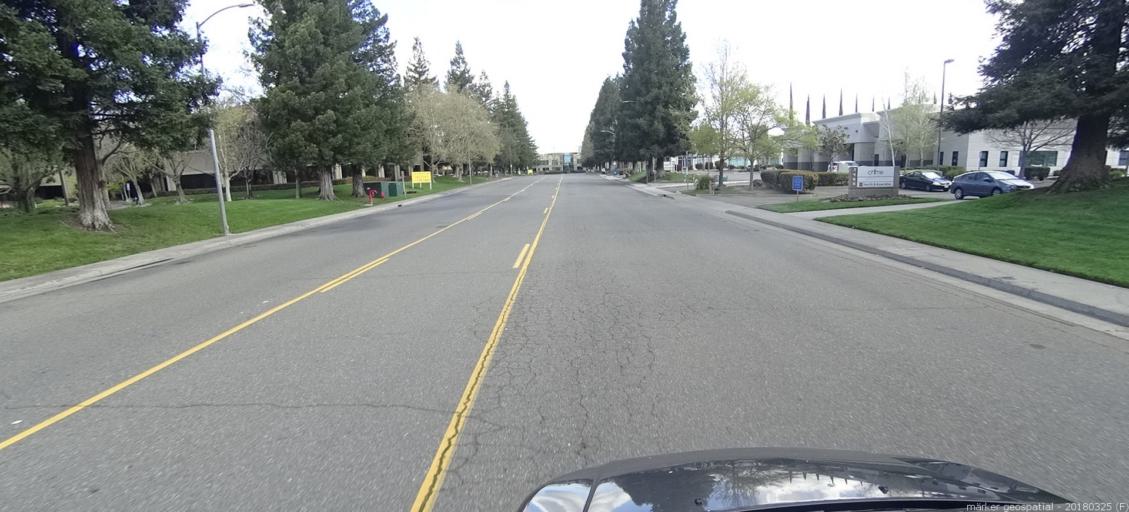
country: US
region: California
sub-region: Sacramento County
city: Sacramento
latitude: 38.6408
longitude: -121.4914
